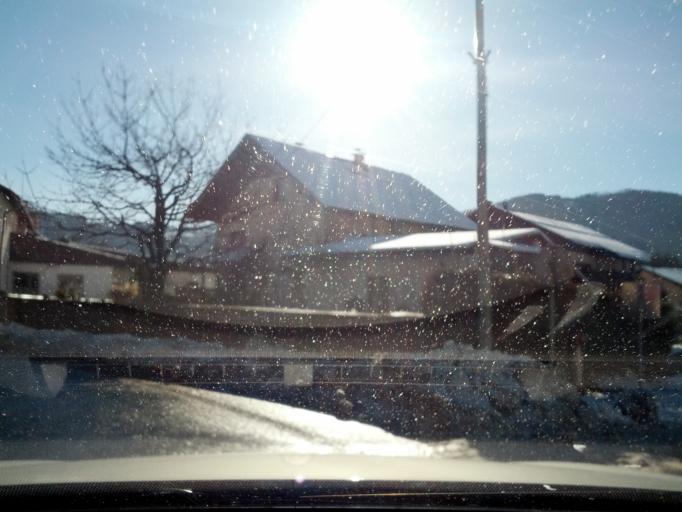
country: SI
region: Moravce
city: Moravce
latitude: 46.1350
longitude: 14.7441
